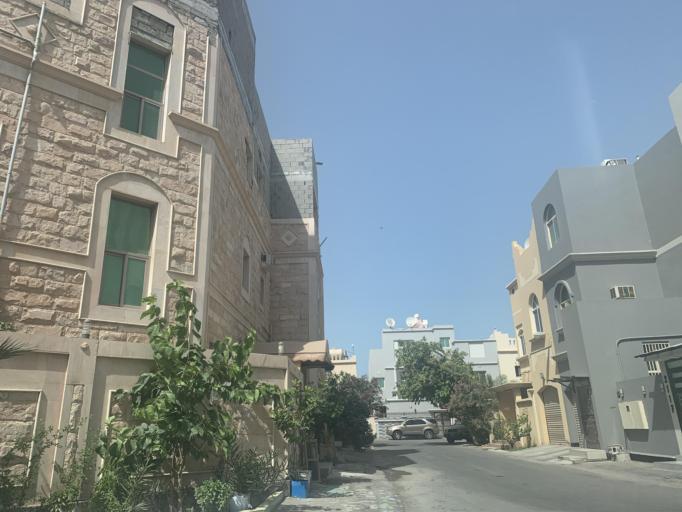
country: BH
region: Northern
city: Sitrah
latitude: 26.1697
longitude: 50.6157
